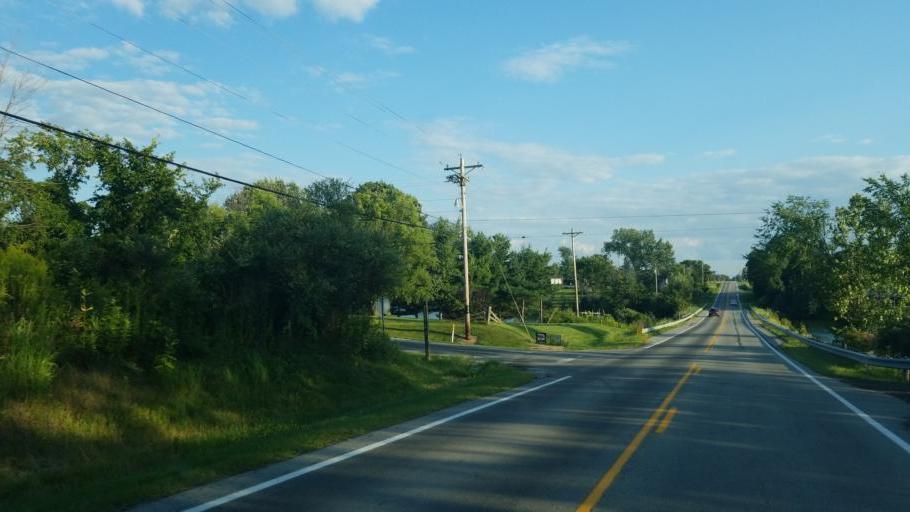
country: US
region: Ohio
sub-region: Huron County
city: Willard
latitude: 41.0947
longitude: -82.7186
